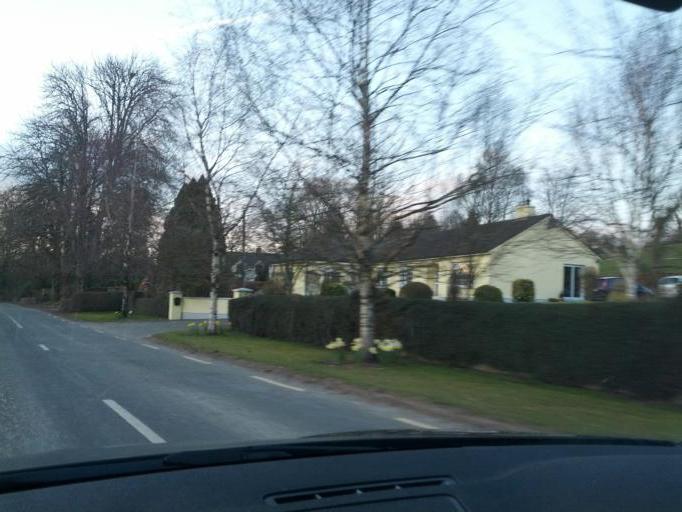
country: IE
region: Munster
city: Nenagh Bridge
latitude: 52.9247
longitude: -8.2261
